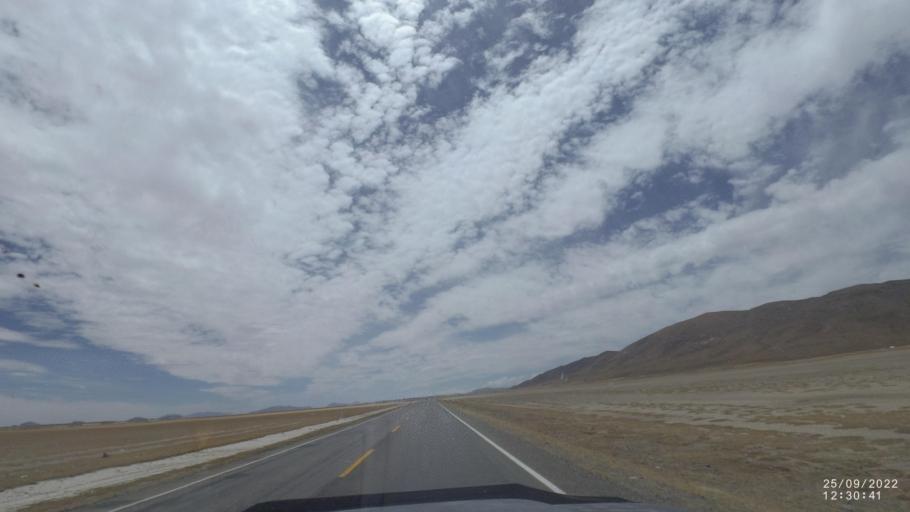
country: BO
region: Oruro
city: Machacamarca
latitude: -18.2462
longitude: -67.0025
